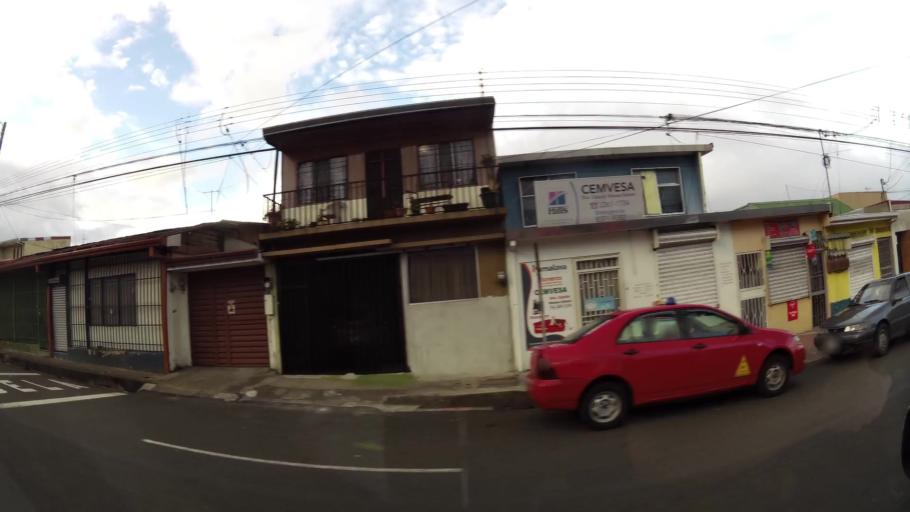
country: CR
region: Heredia
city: Heredia
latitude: 10.0029
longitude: -84.1147
